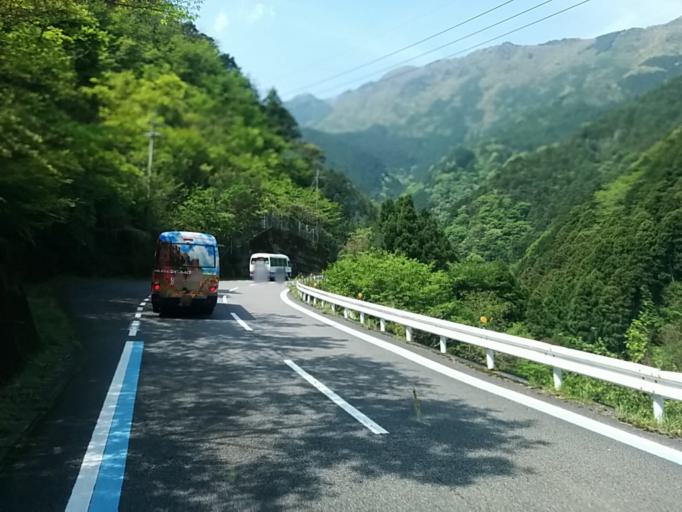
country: JP
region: Ehime
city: Niihama
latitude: 33.8818
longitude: 133.3003
